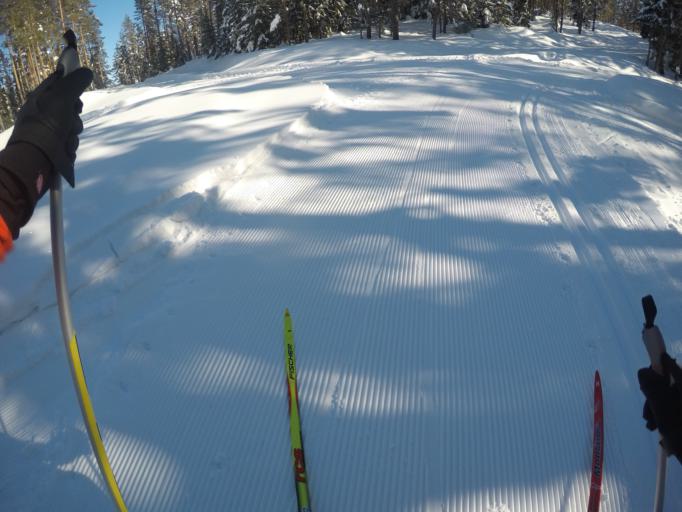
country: SE
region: Vaesternorrland
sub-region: Sundsvalls Kommun
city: Sundsvall
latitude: 62.3670
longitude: 17.2938
